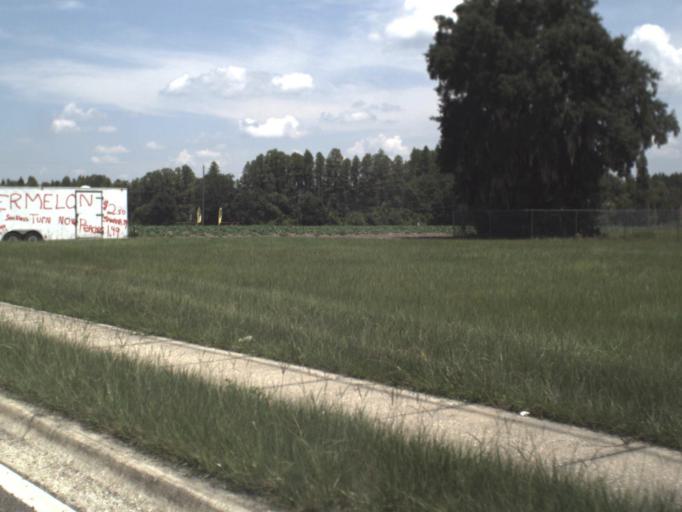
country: US
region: Florida
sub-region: Hillsborough County
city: Lutz
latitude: 28.1585
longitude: -82.4605
